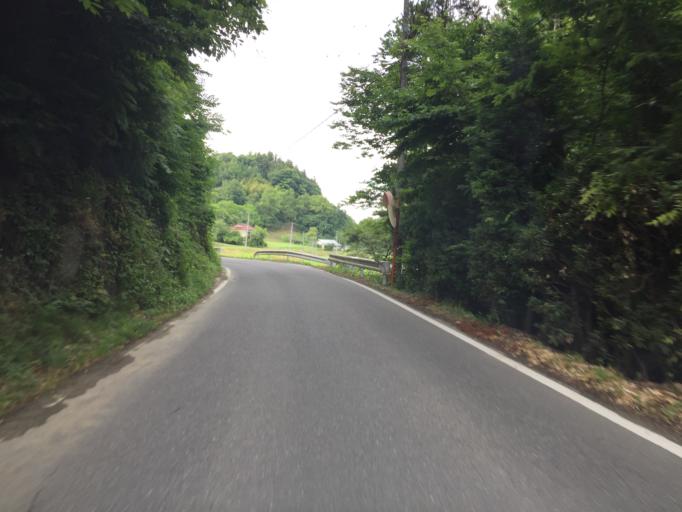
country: JP
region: Fukushima
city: Funehikimachi-funehiki
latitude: 37.4921
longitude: 140.5472
